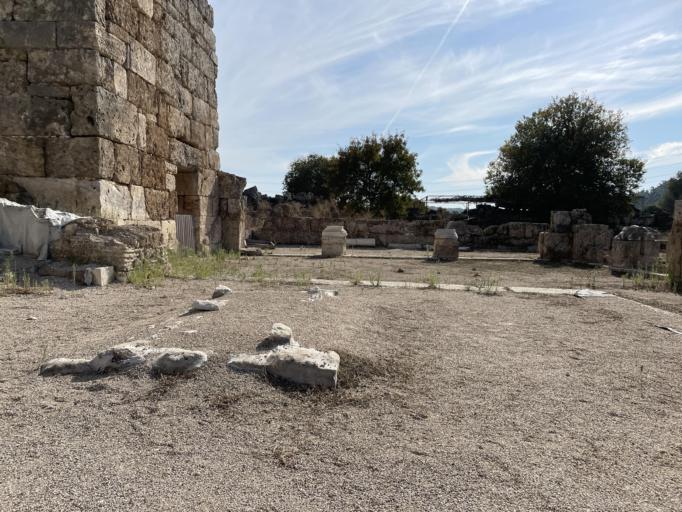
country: TR
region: Antalya
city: Aksu
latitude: 36.9606
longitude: 30.8551
